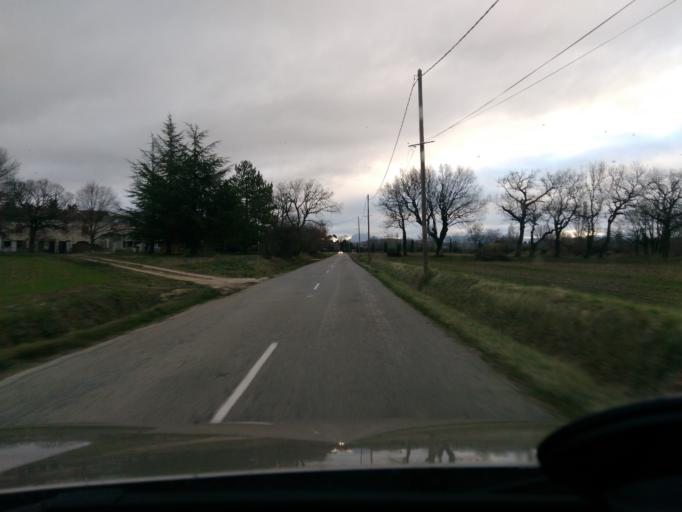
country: FR
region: Rhone-Alpes
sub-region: Departement de la Drome
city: Sauzet
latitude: 44.5750
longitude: 4.8357
